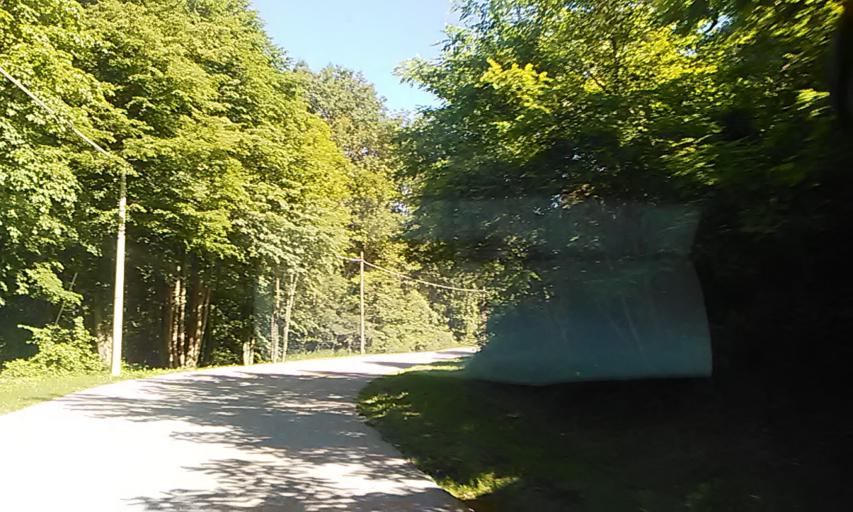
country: IT
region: Piedmont
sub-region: Provincia di Vercelli
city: Varallo
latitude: 45.8298
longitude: 8.2775
